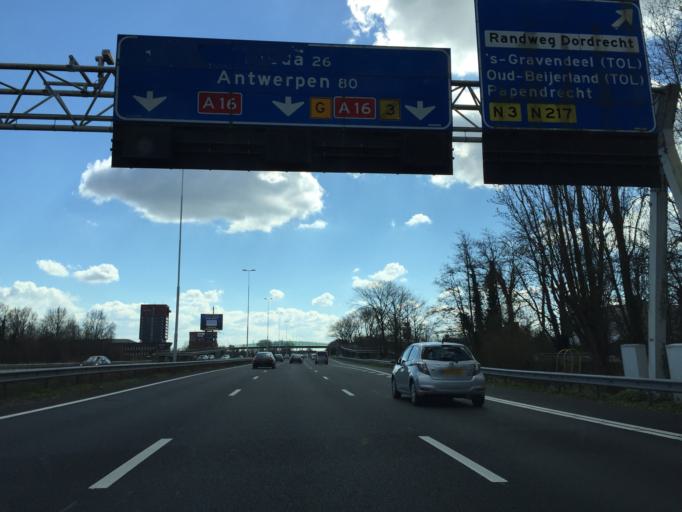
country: NL
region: South Holland
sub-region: Gemeente Dordrecht
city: Dordrecht
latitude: 51.7799
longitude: 4.6504
